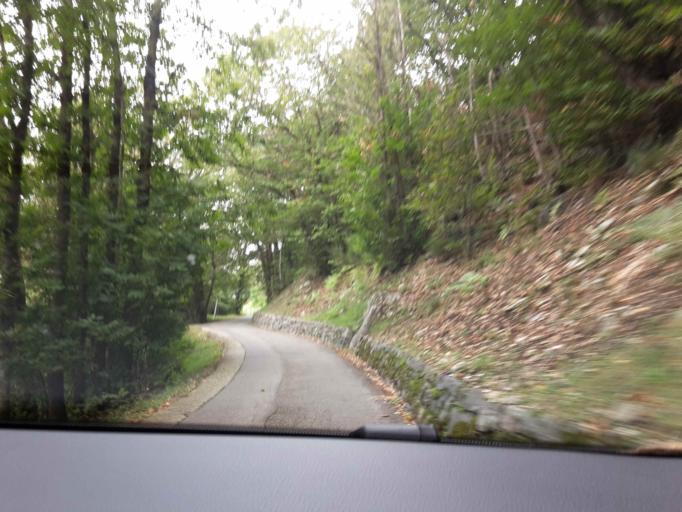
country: CH
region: Ticino
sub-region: Bellinzona District
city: Sementina
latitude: 46.1845
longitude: 8.9787
